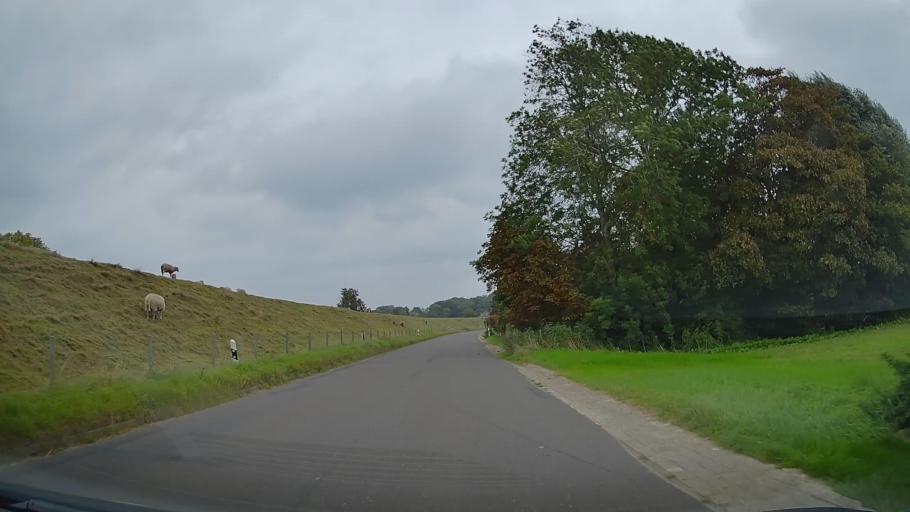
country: DE
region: Lower Saxony
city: Geversdorf
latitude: 53.8244
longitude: 9.0750
